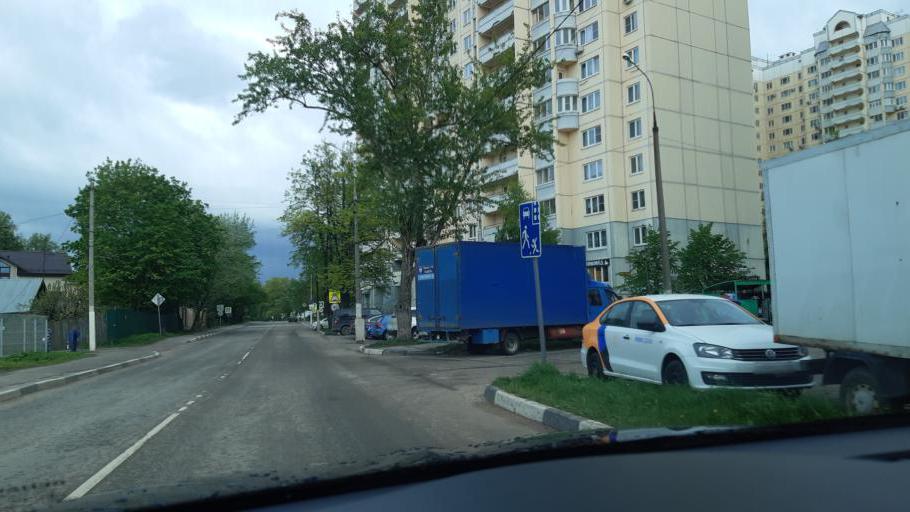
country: RU
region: Moskovskaya
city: Dolgoprudnyy
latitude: 55.9526
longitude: 37.4959
